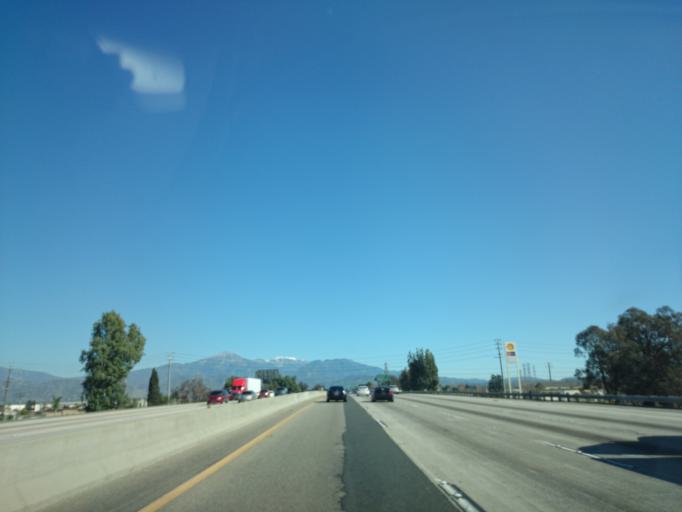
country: US
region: California
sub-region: San Bernardino County
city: Loma Linda
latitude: 34.0666
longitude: -117.2462
